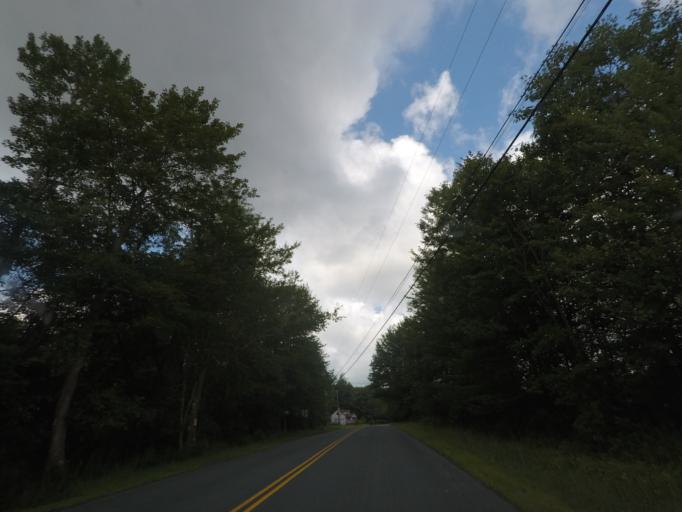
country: US
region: New York
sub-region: Rensselaer County
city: Averill Park
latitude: 42.6376
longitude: -73.4620
